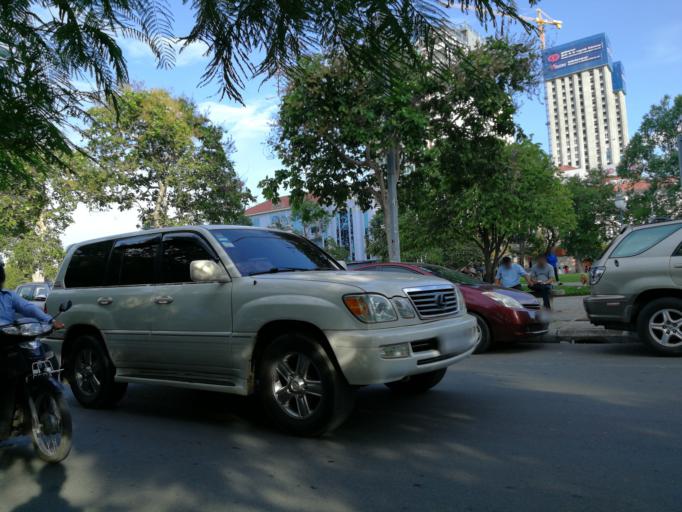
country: KH
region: Phnom Penh
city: Phnom Penh
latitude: 11.5737
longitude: 104.9223
